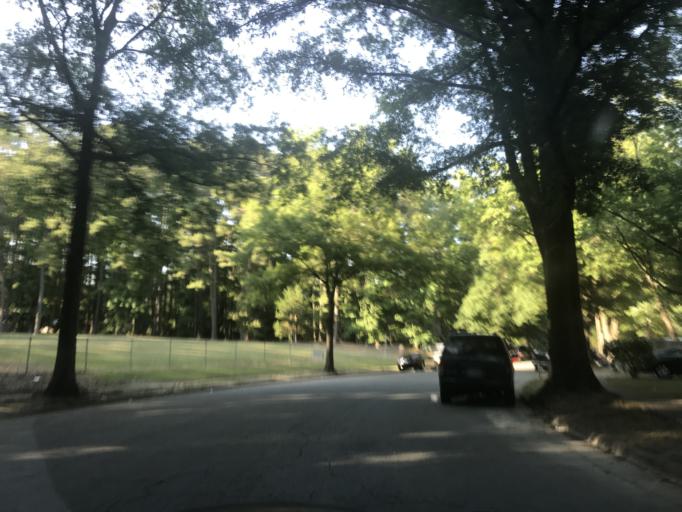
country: US
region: North Carolina
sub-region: Wake County
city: Garner
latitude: 35.7440
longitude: -78.6186
